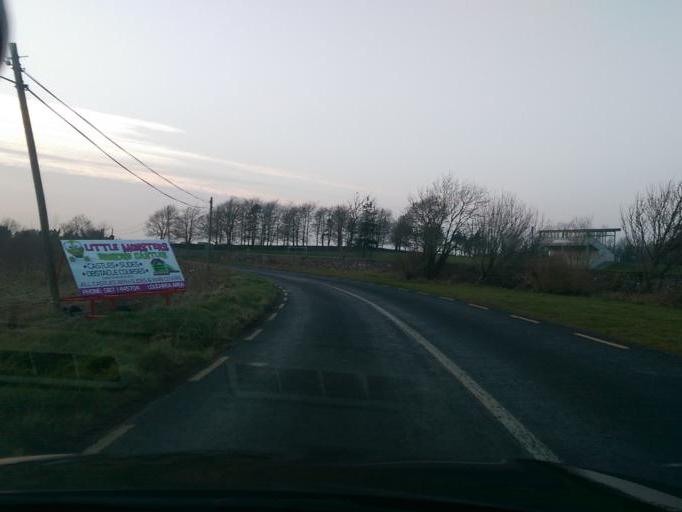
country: IE
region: Connaught
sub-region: County Galway
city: Loughrea
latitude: 53.2272
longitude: -8.6299
